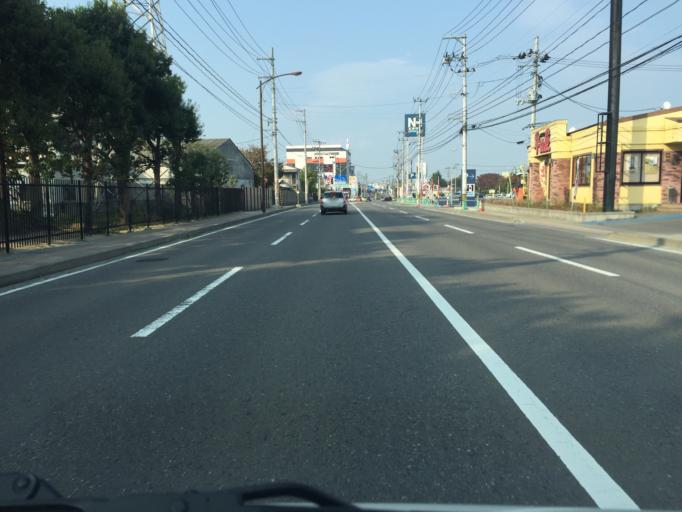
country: JP
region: Fukushima
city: Koriyama
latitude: 37.3982
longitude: 140.3960
